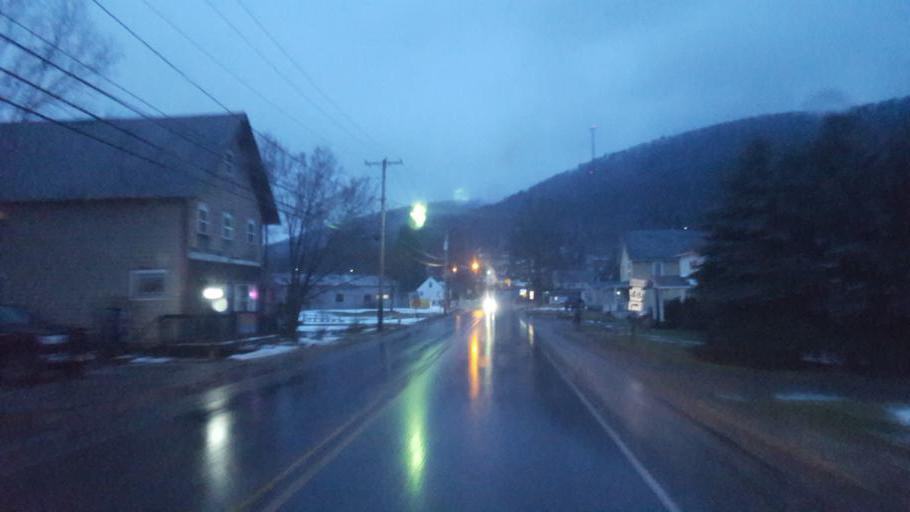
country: US
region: Pennsylvania
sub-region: McKean County
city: Smethport
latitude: 41.8108
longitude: -78.4322
